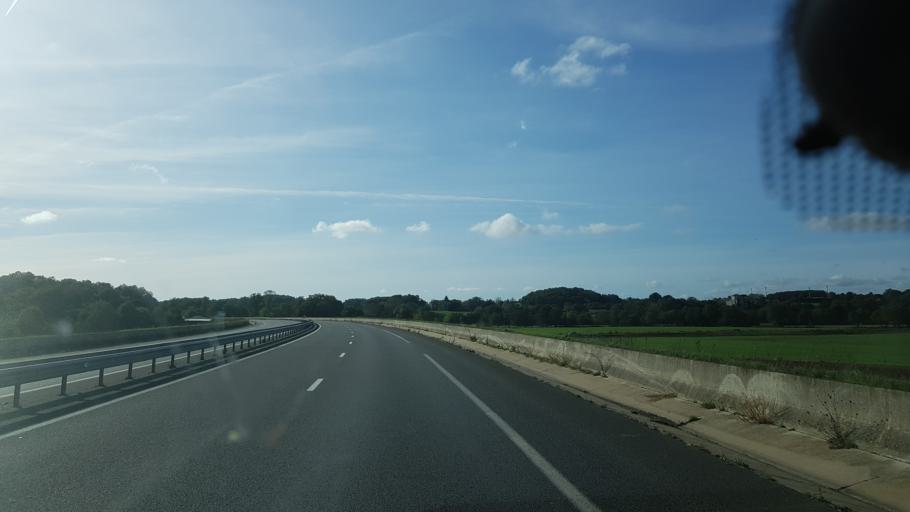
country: FR
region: Poitou-Charentes
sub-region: Departement de la Charente
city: Rivieres
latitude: 45.7524
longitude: 0.3748
